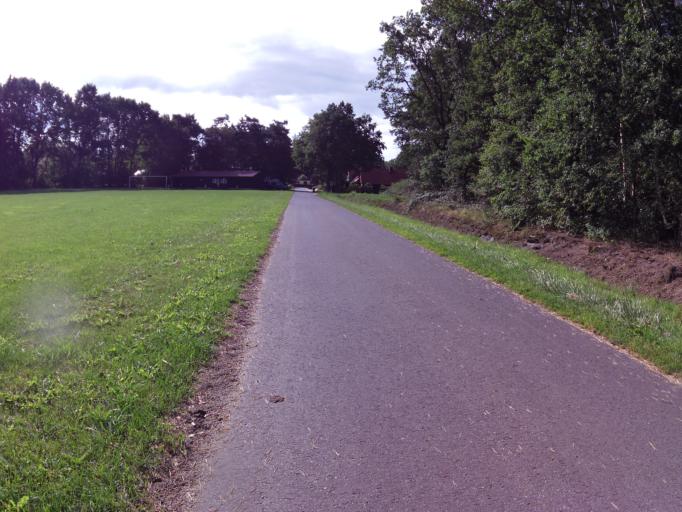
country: DE
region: Lower Saxony
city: Sandbostel
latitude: 53.4345
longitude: 9.1239
